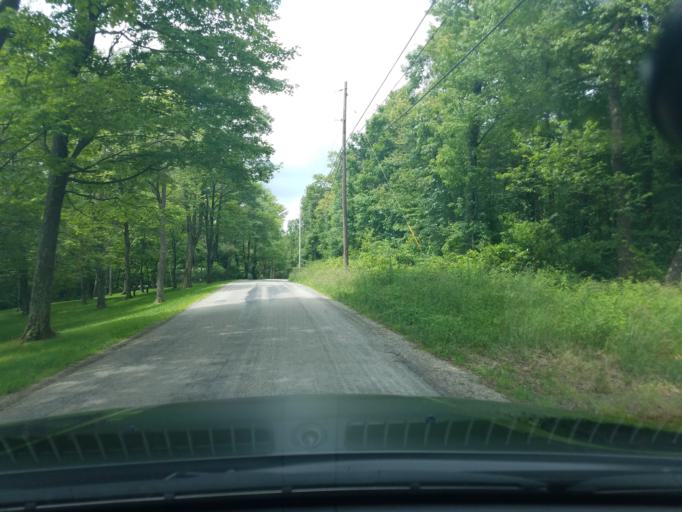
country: US
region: Pennsylvania
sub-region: Fayette County
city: Bear Rocks
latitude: 40.1792
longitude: -79.4083
